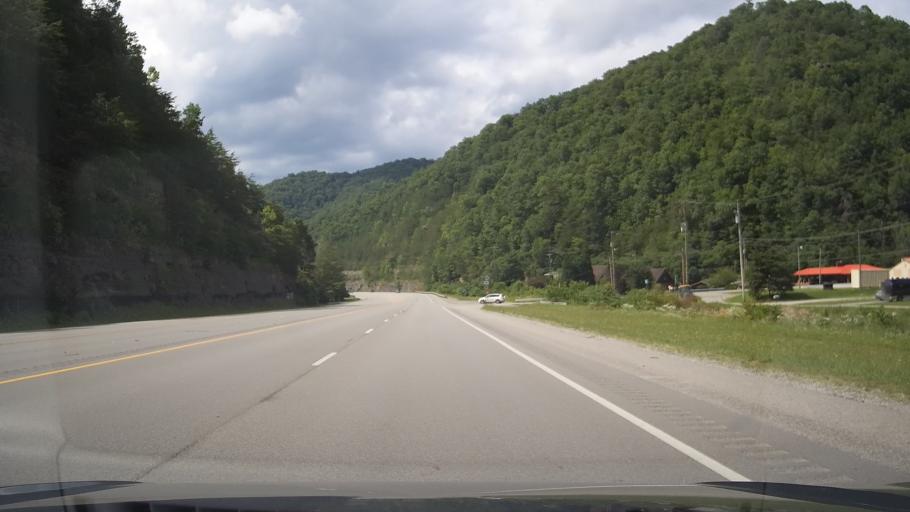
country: US
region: Kentucky
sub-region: Letcher County
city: Jenkins
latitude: 37.3134
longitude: -82.5489
